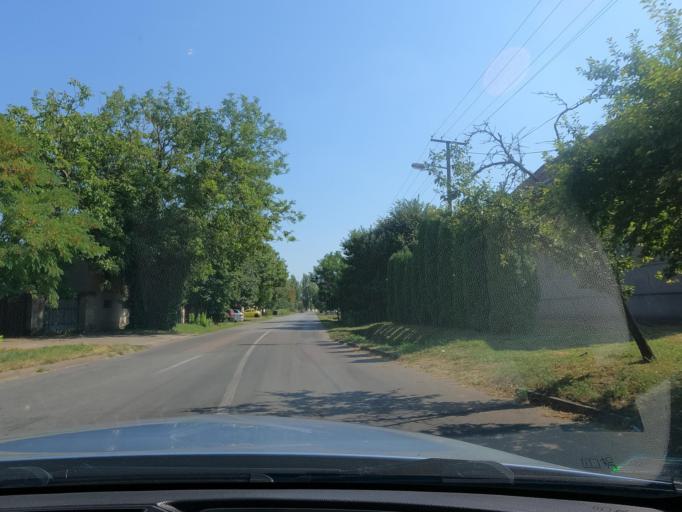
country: RS
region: Autonomna Pokrajina Vojvodina
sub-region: Severnobacki Okrug
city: Backa Topola
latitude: 45.8151
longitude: 19.6442
